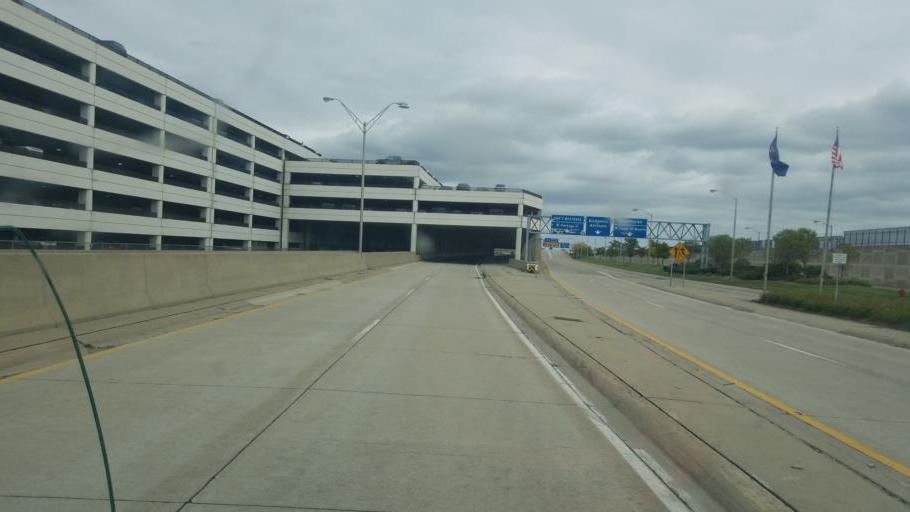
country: US
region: Michigan
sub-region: Wayne County
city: Romulus
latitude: 42.2048
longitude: -83.3564
